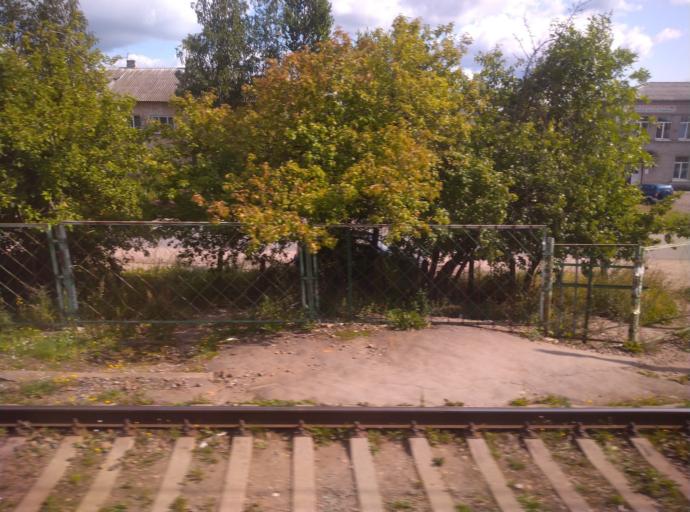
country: RU
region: Leningrad
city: Ul'yanovka
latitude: 59.6341
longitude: 30.7596
